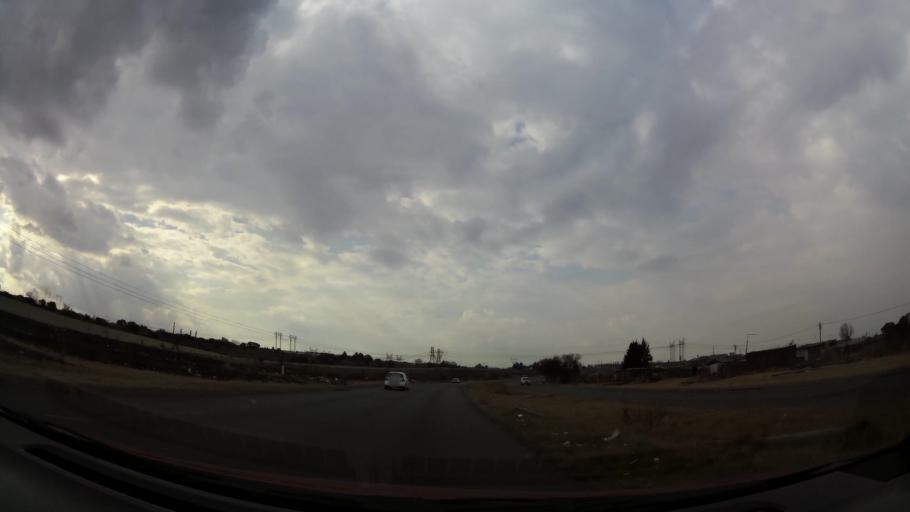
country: ZA
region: Gauteng
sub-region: Sedibeng District Municipality
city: Vanderbijlpark
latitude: -26.6691
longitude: 27.8378
